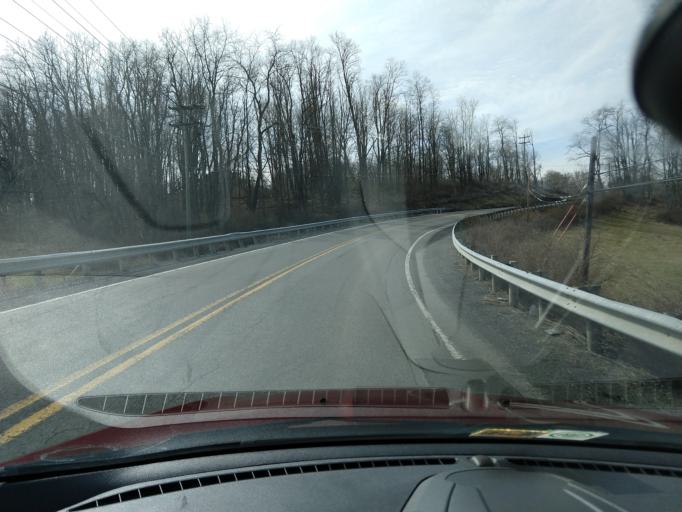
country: US
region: West Virginia
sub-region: Greenbrier County
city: Lewisburg
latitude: 37.8763
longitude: -80.4112
